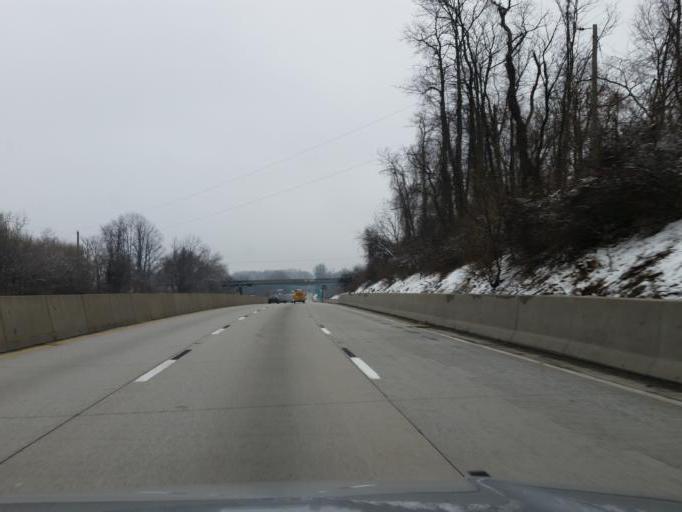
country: US
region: Pennsylvania
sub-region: Dauphin County
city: Steelton
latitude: 40.1917
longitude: -76.8501
